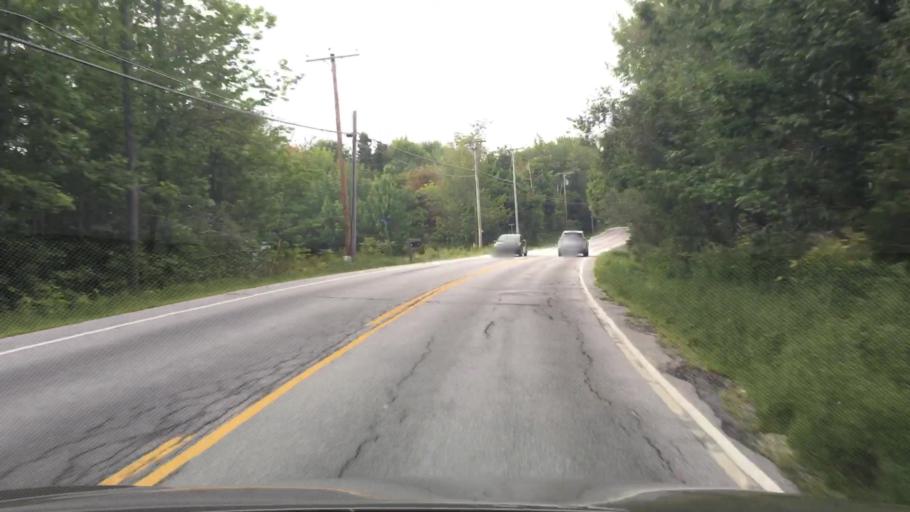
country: US
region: Maine
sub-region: Hancock County
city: Penobscot
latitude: 44.4319
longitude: -68.6057
